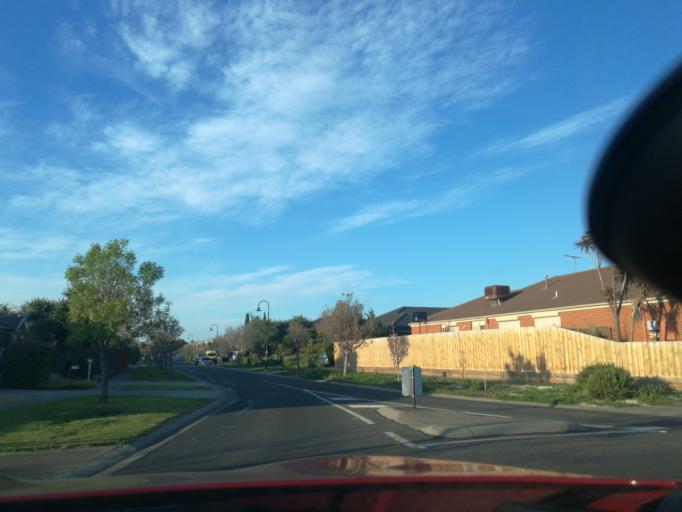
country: AU
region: Victoria
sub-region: Wyndham
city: Williams Landing
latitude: -37.8805
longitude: 144.7424
